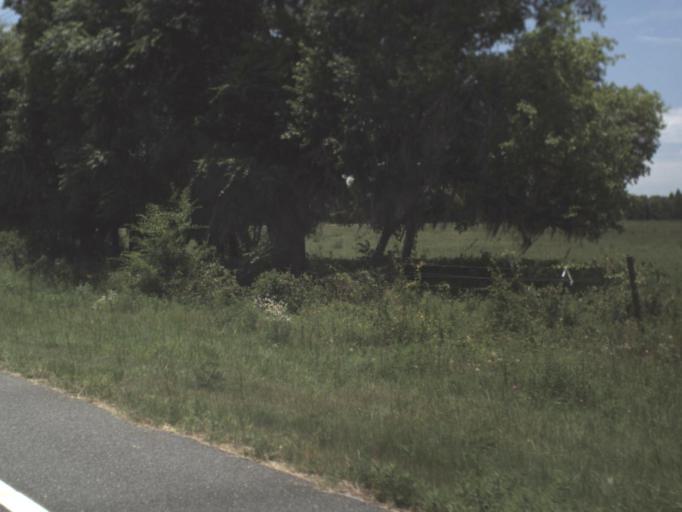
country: US
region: Florida
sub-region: Dixie County
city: Cross City
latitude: 29.7829
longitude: -82.9759
